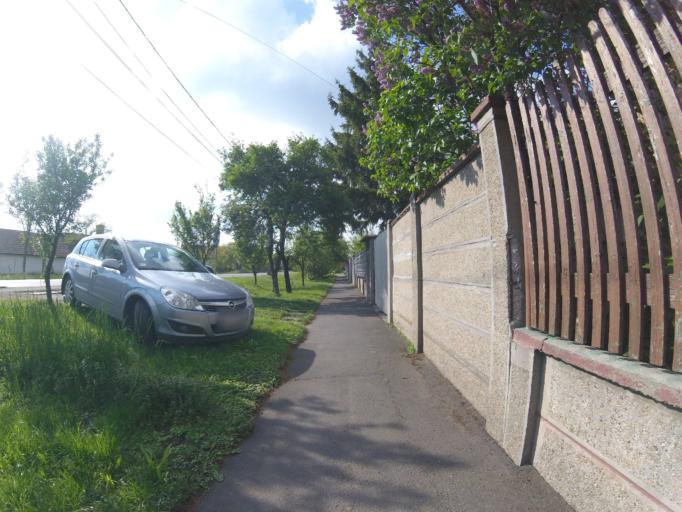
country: HU
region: Jasz-Nagykun-Szolnok
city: Jaszbereny
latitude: 47.5130
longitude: 19.9050
